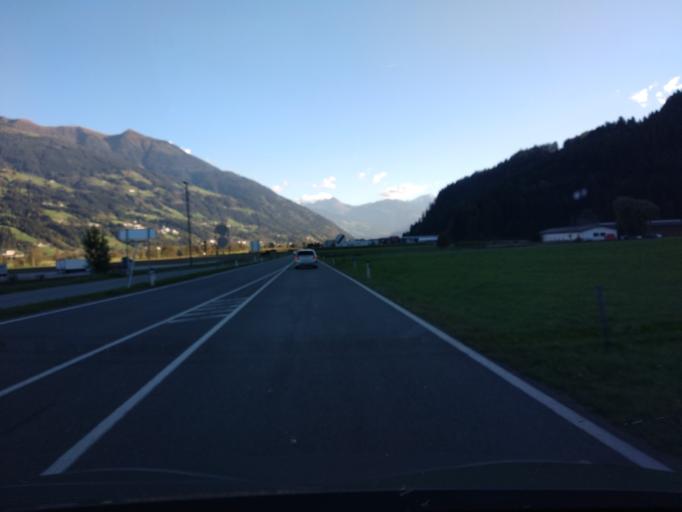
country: AT
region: Tyrol
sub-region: Politischer Bezirk Schwaz
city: Schlitters
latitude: 47.3742
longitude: 11.8451
